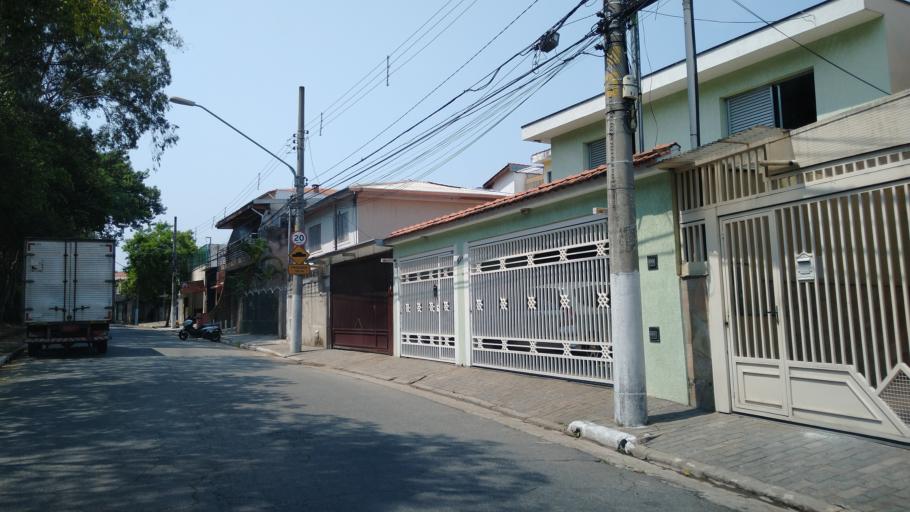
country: BR
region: Sao Paulo
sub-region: Sao Paulo
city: Sao Paulo
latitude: -23.4972
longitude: -46.6074
